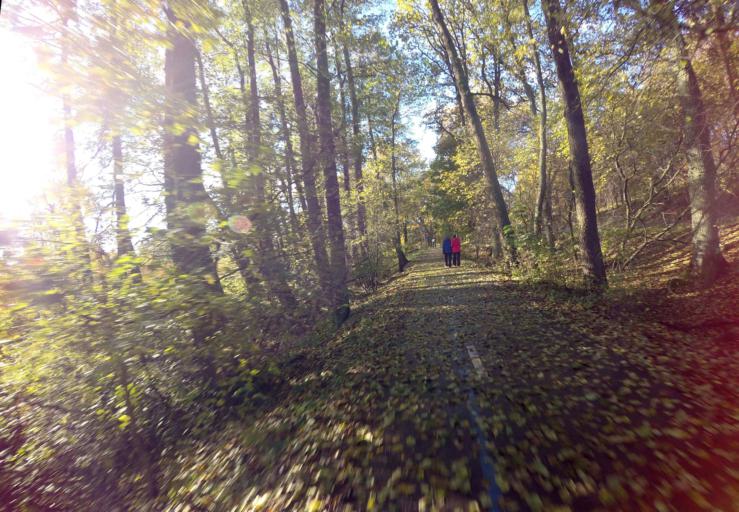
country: FI
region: Varsinais-Suomi
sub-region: Turku
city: Raisio
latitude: 60.4394
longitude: 22.2033
